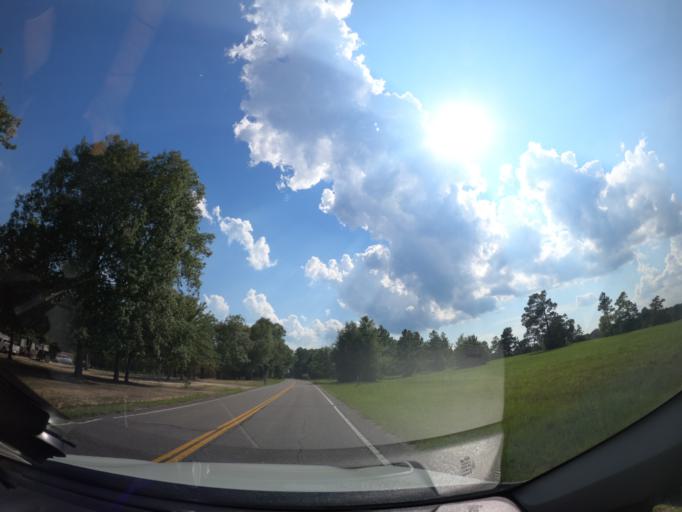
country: US
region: South Carolina
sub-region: Barnwell County
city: Williston
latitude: 33.5209
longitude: -81.5004
